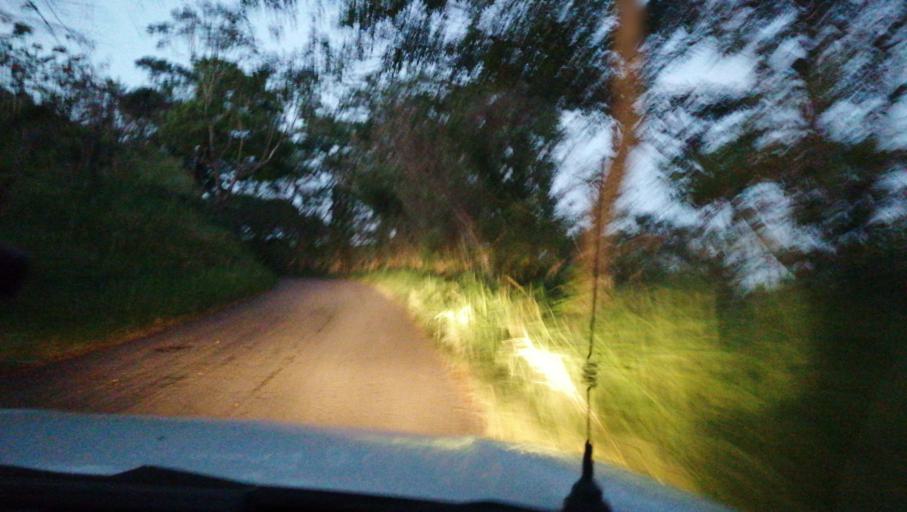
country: MX
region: Chiapas
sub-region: Ostuacan
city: Nuevo Juan del Grijalva
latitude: 17.4751
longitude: -93.3460
